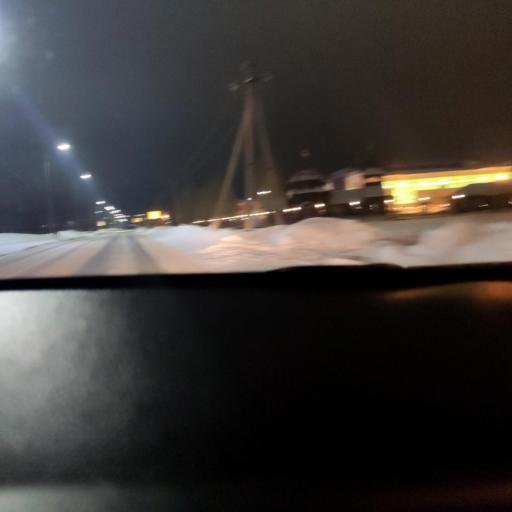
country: RU
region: Tatarstan
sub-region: Chistopol'skiy Rayon
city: Chistopol'
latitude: 55.3618
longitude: 50.5819
